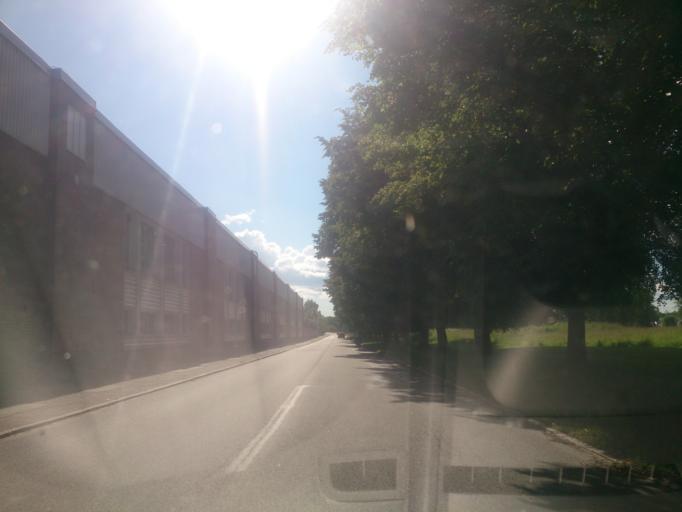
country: SE
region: OEstergoetland
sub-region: Norrkopings Kommun
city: Norrkoping
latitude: 58.5993
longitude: 16.1374
